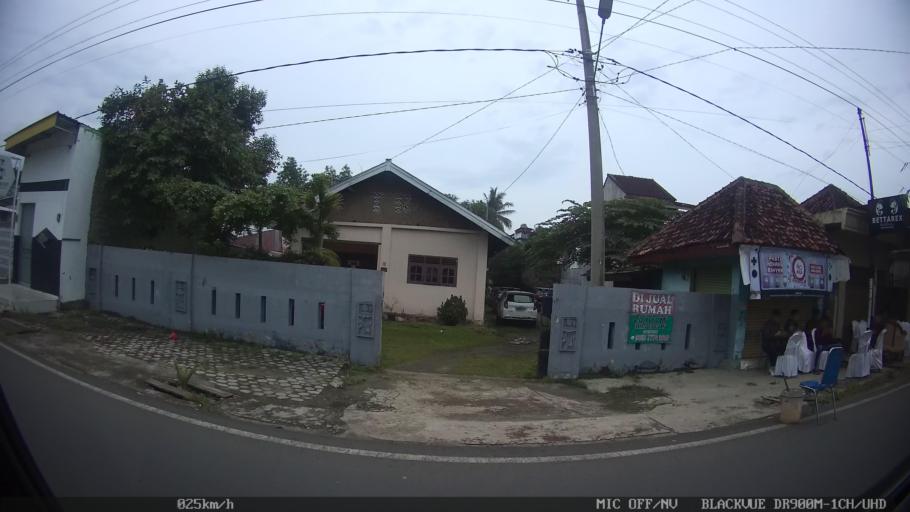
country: ID
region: Lampung
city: Kedaton
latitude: -5.3865
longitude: 105.2452
